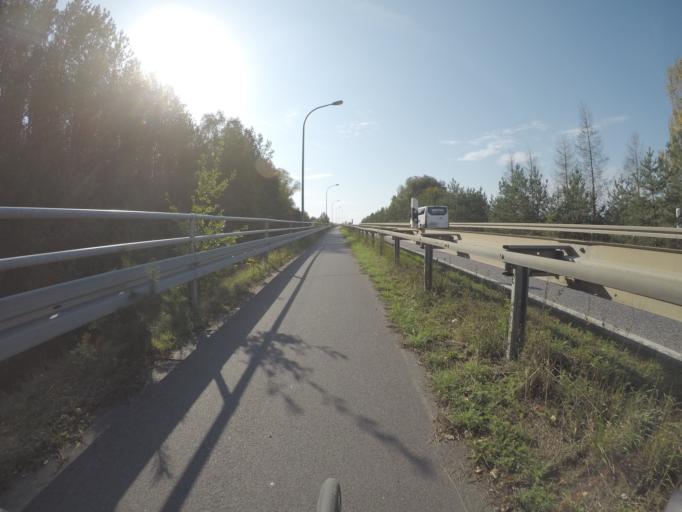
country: DE
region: Brandenburg
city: Leegebruch
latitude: 52.6972
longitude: 13.2046
